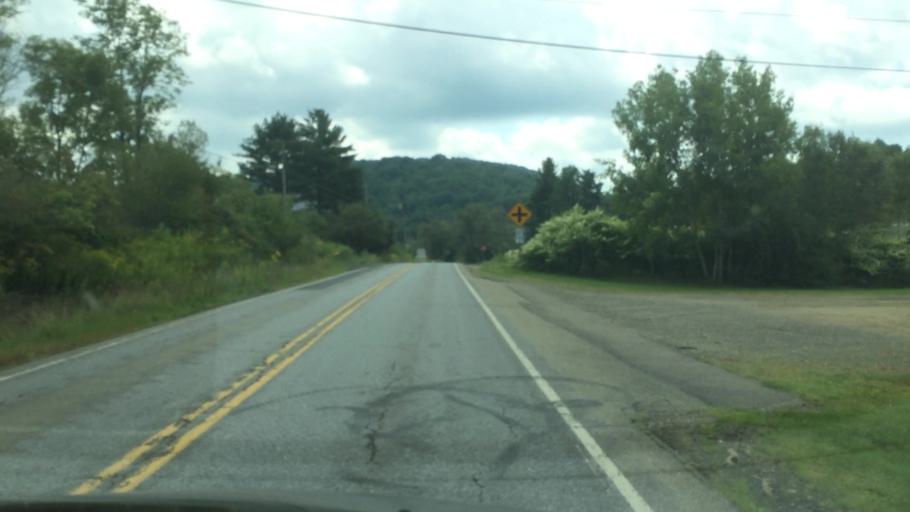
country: US
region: Pennsylvania
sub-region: McKean County
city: Bradford
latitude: 41.9145
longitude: -78.6425
